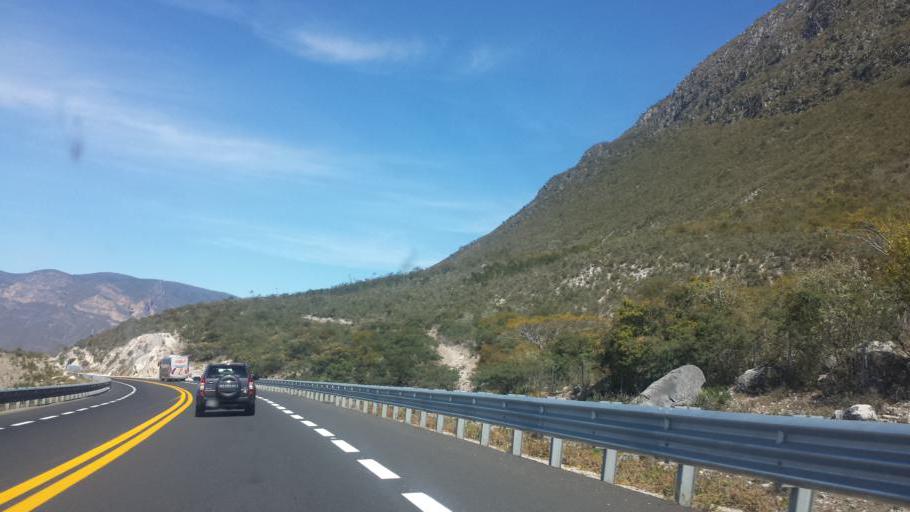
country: MX
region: Puebla
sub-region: San Jose Miahuatlan
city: San Pedro Tetitlan
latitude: 18.0708
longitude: -97.3522
